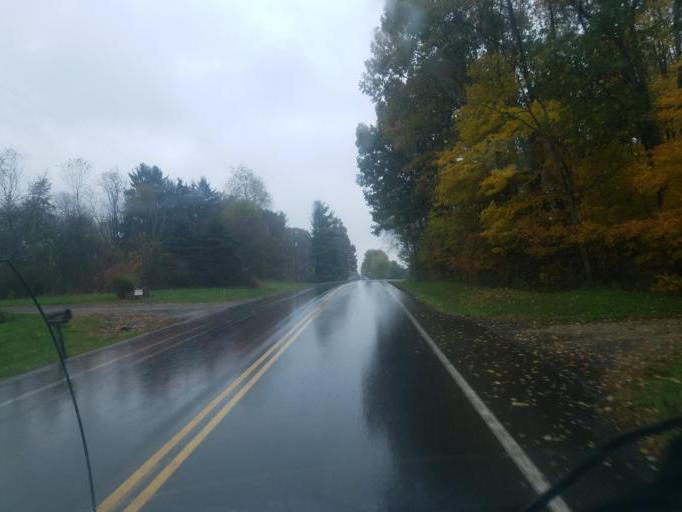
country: US
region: Ohio
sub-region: Licking County
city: Utica
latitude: 40.2550
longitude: -82.3334
